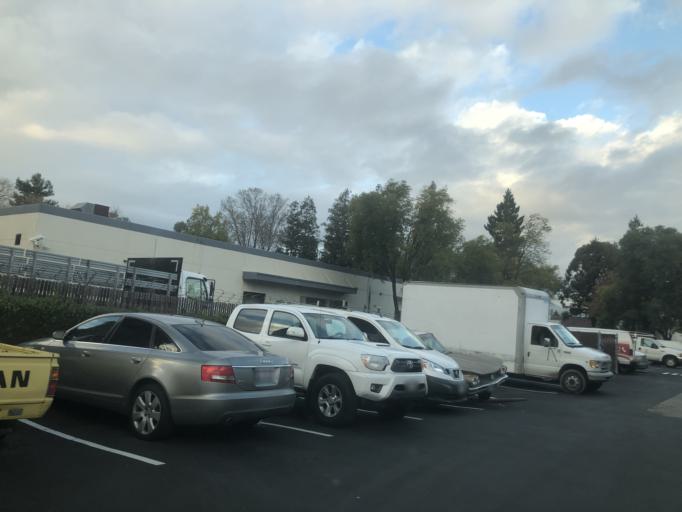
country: US
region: California
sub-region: Santa Clara County
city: Santa Clara
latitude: 37.3766
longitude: -121.9185
